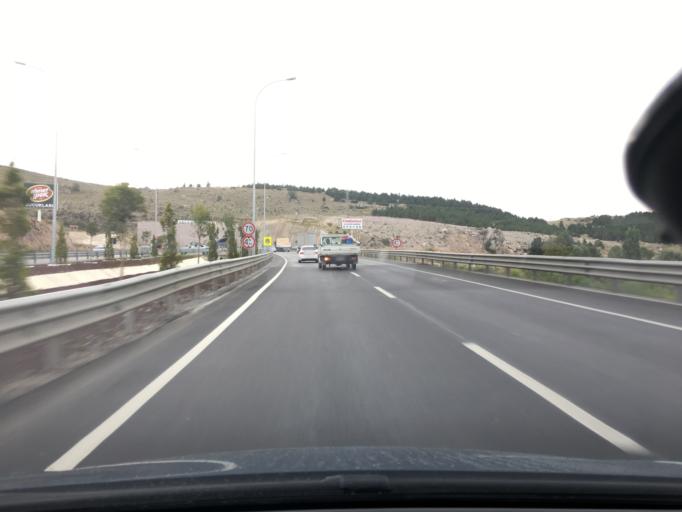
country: TR
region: Afyonkarahisar
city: Afyonkarahisar
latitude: 38.7951
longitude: 30.4400
